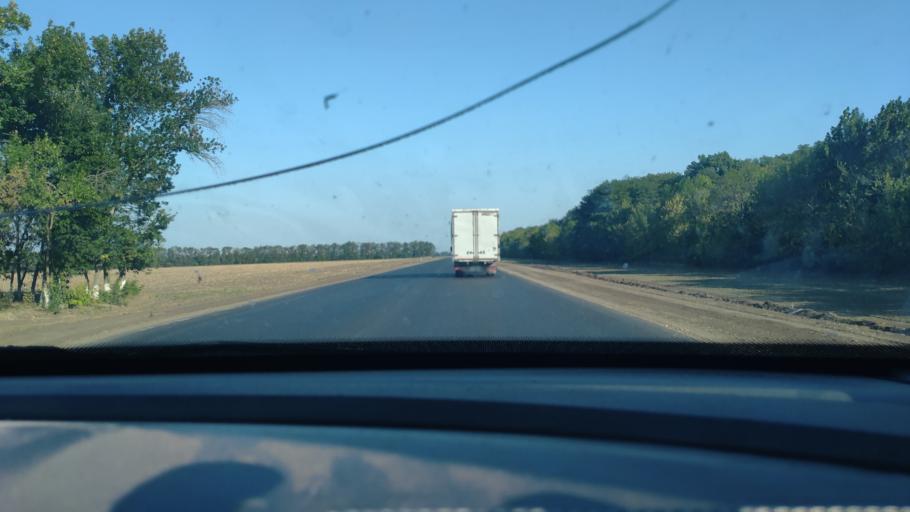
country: RU
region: Krasnodarskiy
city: Staroshcherbinovskaya
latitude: 46.5817
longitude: 38.8275
